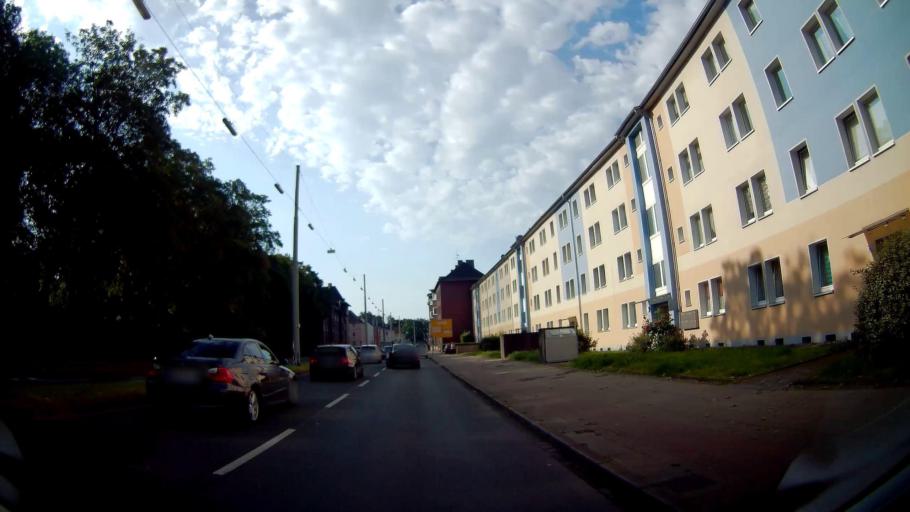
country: DE
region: North Rhine-Westphalia
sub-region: Regierungsbezirk Arnsberg
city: Herne
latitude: 51.5365
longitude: 7.2183
